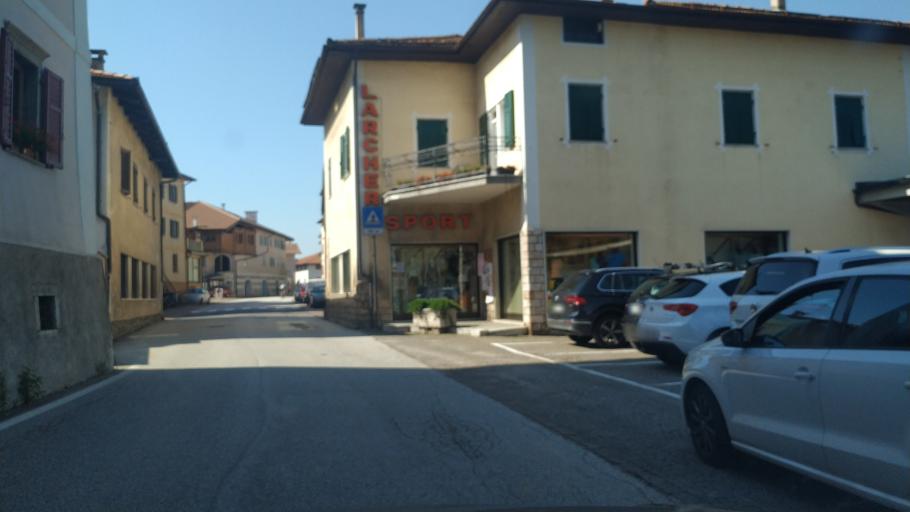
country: IT
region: Trentino-Alto Adige
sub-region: Provincia di Trento
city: Cavareno
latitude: 46.4092
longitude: 11.1374
